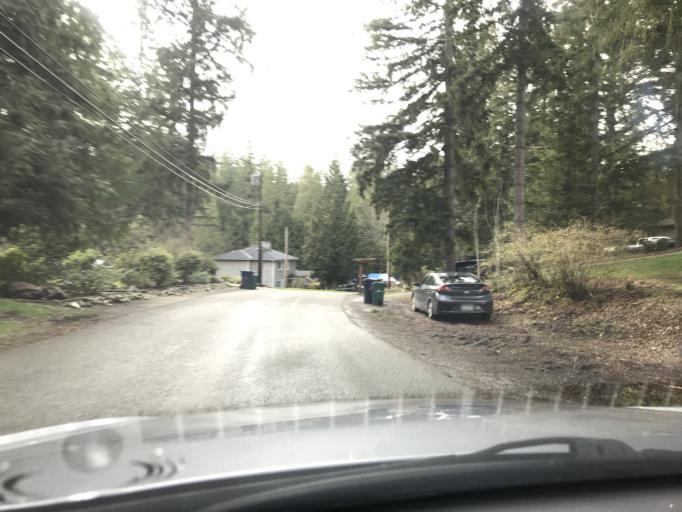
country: US
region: Washington
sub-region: King County
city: Ames Lake
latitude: 47.6377
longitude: -121.9667
